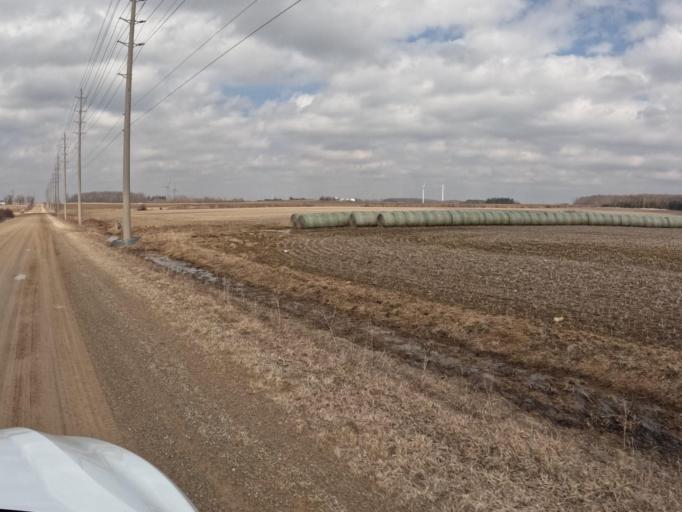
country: CA
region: Ontario
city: Shelburne
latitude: 44.0482
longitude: -80.3193
